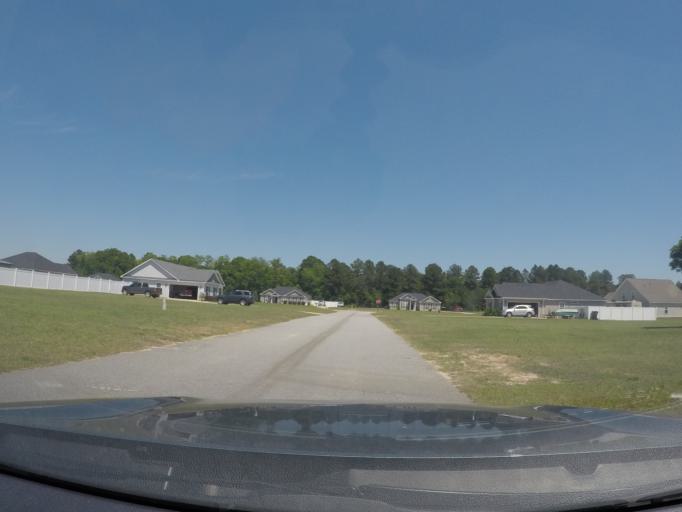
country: US
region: Georgia
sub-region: Bulloch County
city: Brooklet
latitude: 32.3513
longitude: -81.7553
